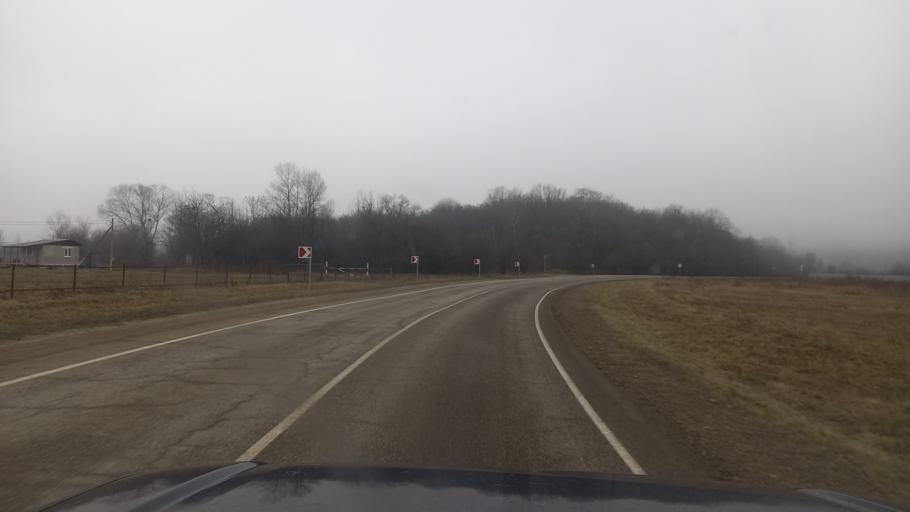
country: RU
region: Krasnodarskiy
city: Neftegorsk
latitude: 44.2876
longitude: 39.8204
